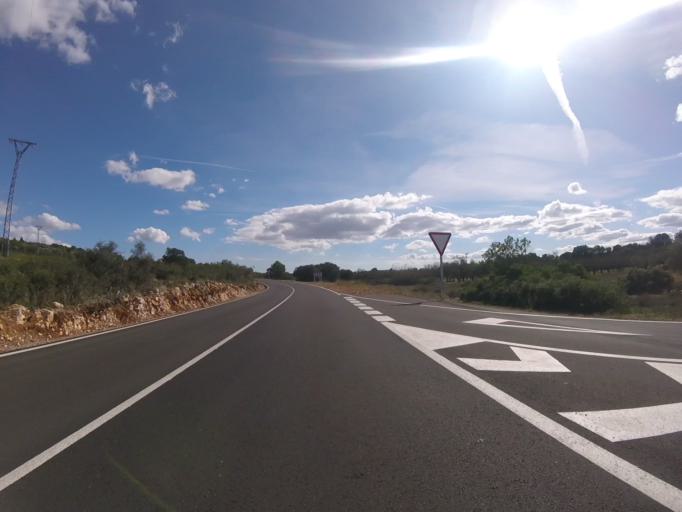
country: ES
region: Valencia
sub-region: Provincia de Castello
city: Albocasser
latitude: 40.4095
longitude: 0.0715
